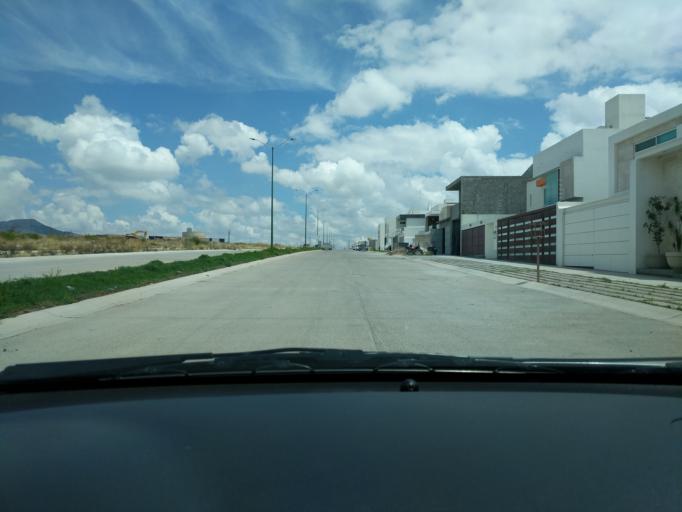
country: MX
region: San Luis Potosi
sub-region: Mexquitic de Carmona
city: Guadalupe Victoria
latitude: 22.1564
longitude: -101.0529
